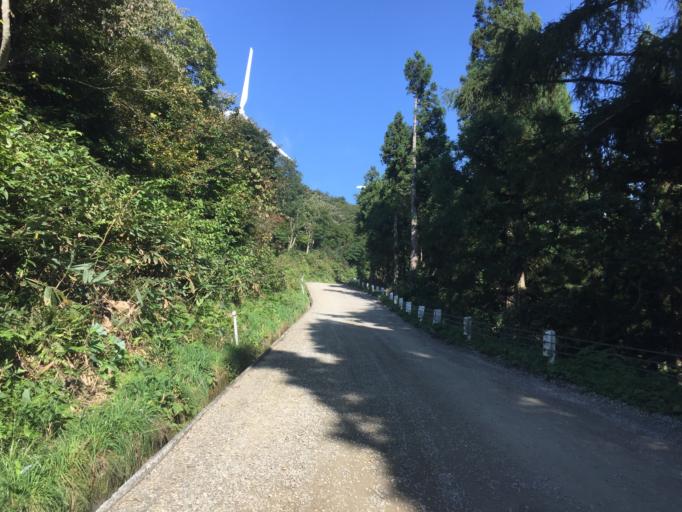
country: JP
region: Fukushima
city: Inawashiro
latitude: 37.4589
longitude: 139.9945
